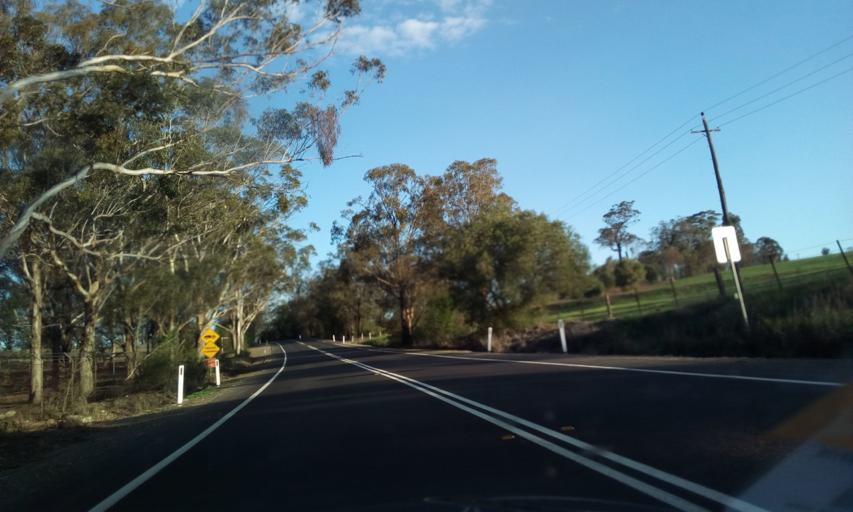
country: AU
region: New South Wales
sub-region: Camden
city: Camden South
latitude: -34.1282
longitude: 150.7035
